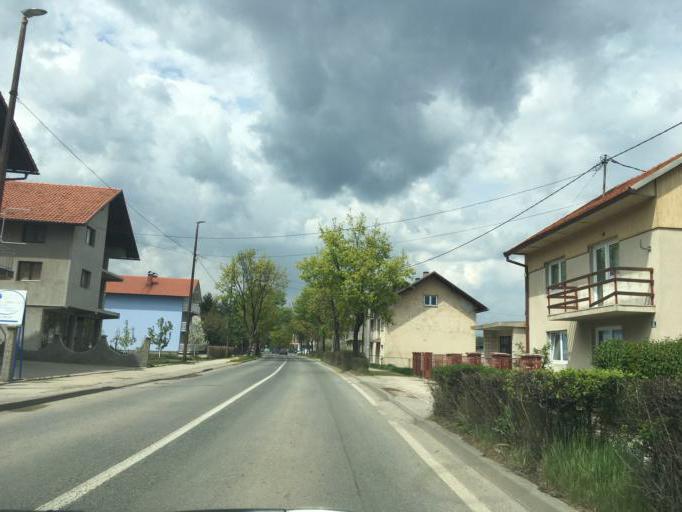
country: BA
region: Federation of Bosnia and Herzegovina
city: Bugojno
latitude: 44.0459
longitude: 17.4482
